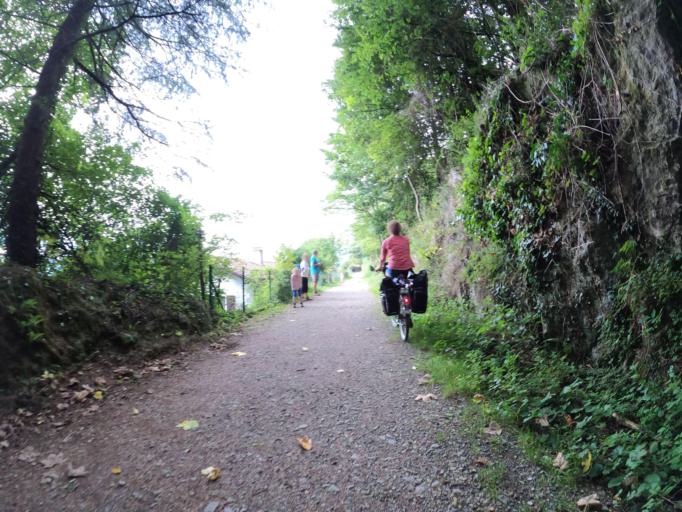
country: ES
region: Navarre
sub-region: Provincia de Navarra
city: Lekunberri
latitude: 43.0040
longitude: -1.8935
